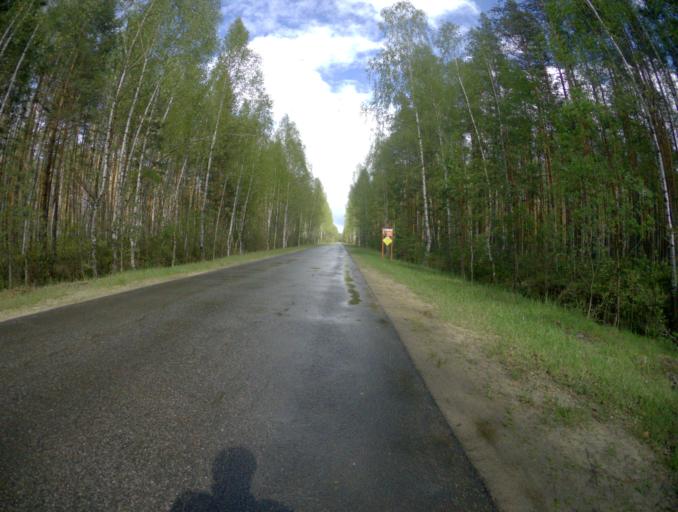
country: RU
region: Vladimir
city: Urshel'skiy
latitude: 55.5820
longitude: 40.1959
